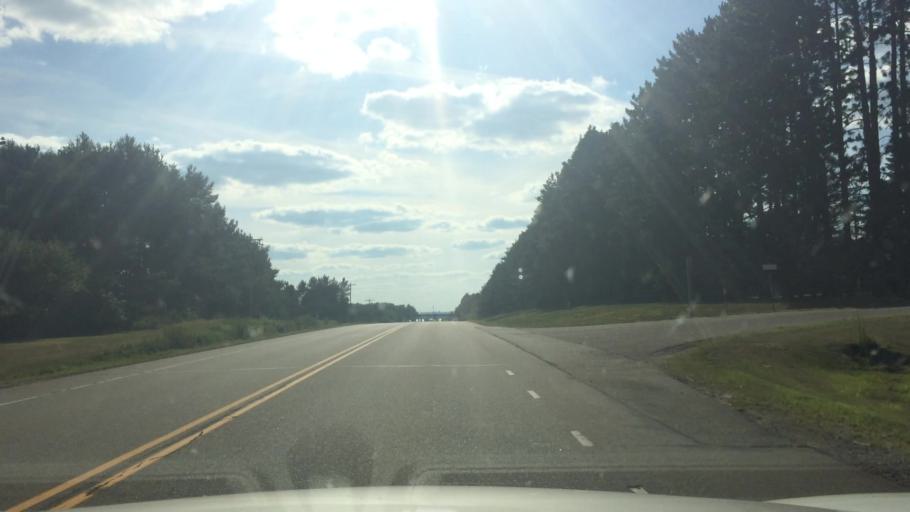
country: US
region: Wisconsin
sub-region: Lincoln County
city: Merrill
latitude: 45.1779
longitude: -89.6326
